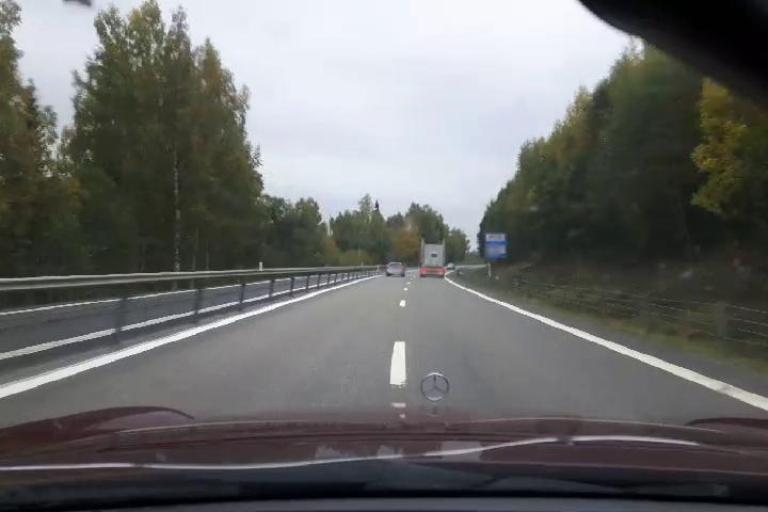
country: SE
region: Vaesternorrland
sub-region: Kramfors Kommun
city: Nordingra
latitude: 63.0607
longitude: 18.3507
